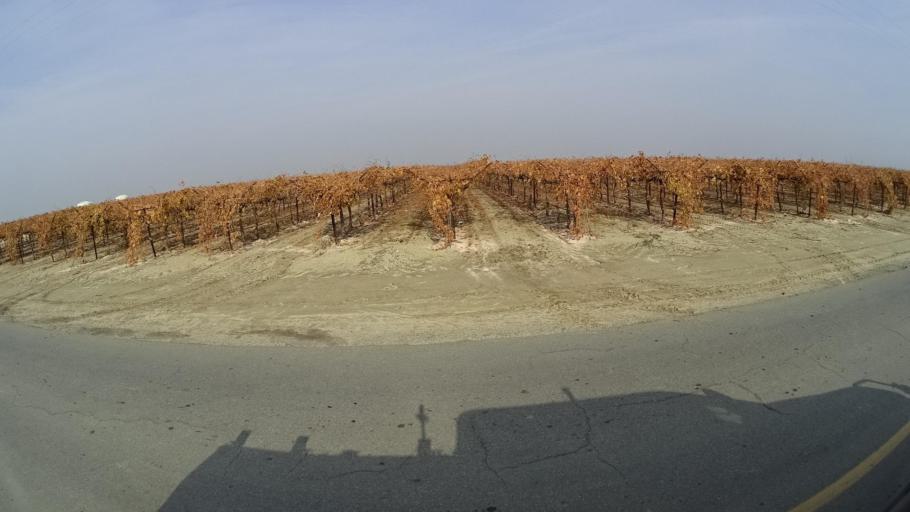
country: US
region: California
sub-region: Kern County
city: Weedpatch
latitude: 35.0744
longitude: -118.9258
